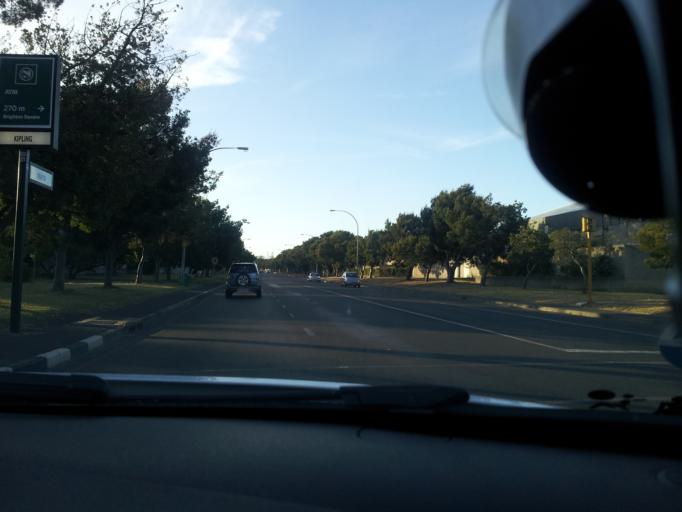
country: ZA
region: Western Cape
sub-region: City of Cape Town
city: Kraaifontein
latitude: -33.8404
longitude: 18.7047
